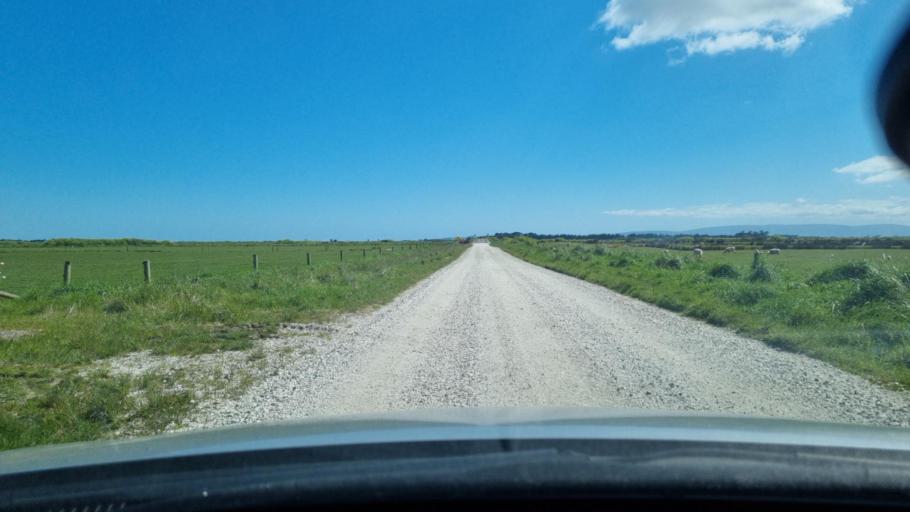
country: NZ
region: Southland
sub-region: Invercargill City
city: Invercargill
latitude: -46.3693
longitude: 168.2550
